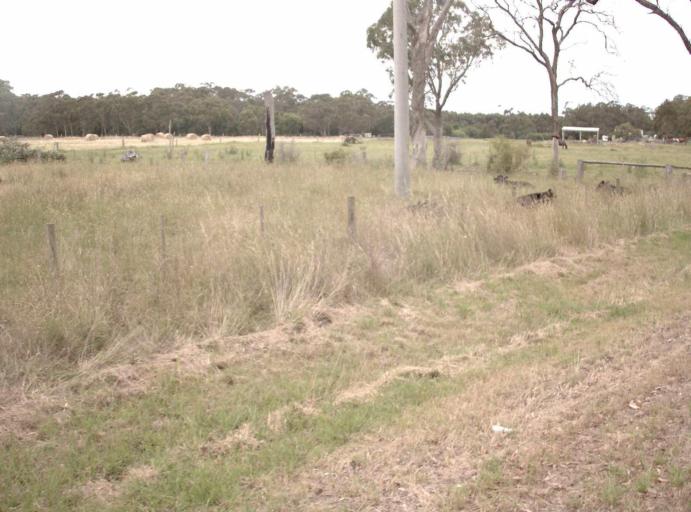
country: AU
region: Victoria
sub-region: Latrobe
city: Traralgon
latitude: -38.5236
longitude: 146.8628
